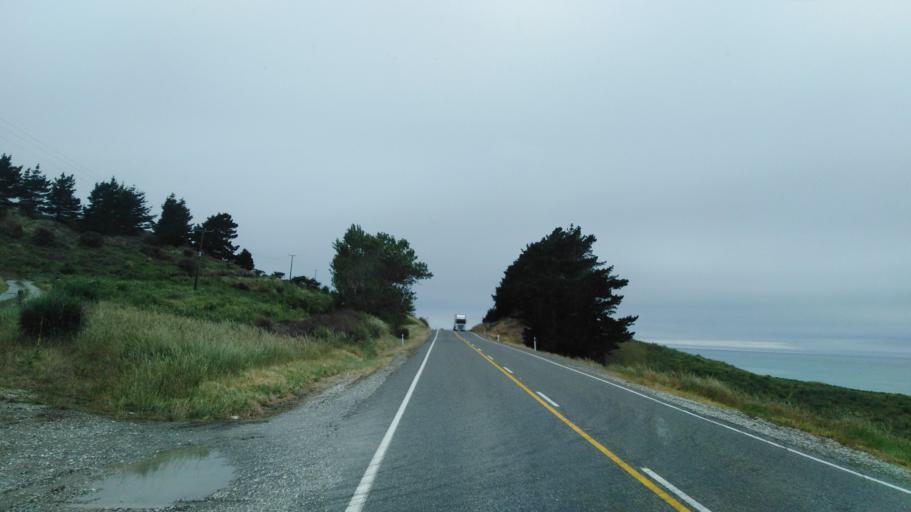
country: NZ
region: Marlborough
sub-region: Marlborough District
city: Blenheim
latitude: -41.9140
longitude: 174.1000
